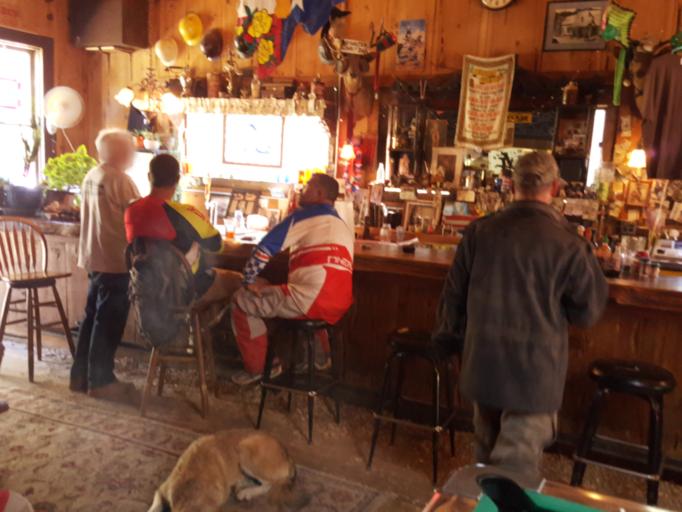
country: US
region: California
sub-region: Sierra County
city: Downieville
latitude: 39.4704
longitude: -120.8434
